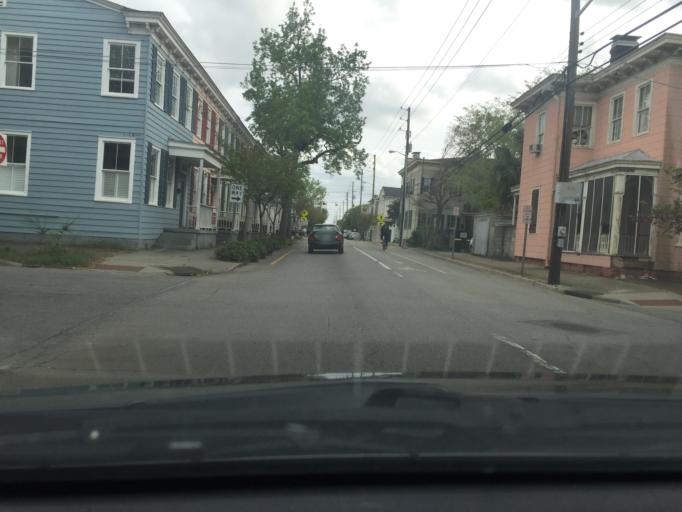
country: US
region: Georgia
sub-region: Chatham County
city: Savannah
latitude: 32.0705
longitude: -81.0893
